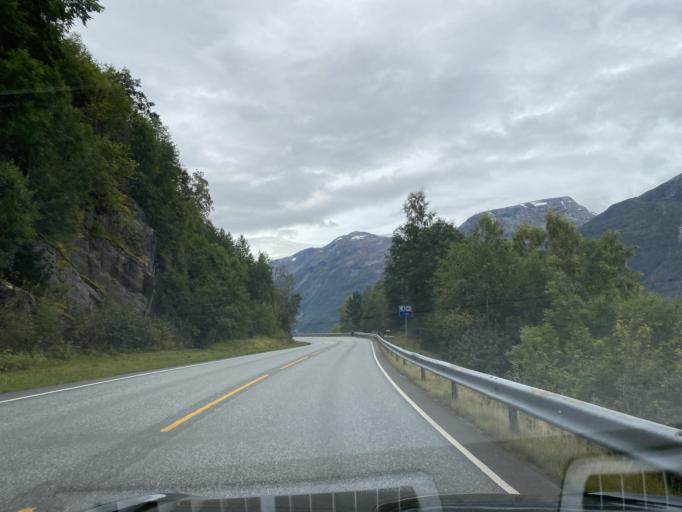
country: NO
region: Hordaland
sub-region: Odda
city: Odda
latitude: 60.1940
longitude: 6.5923
